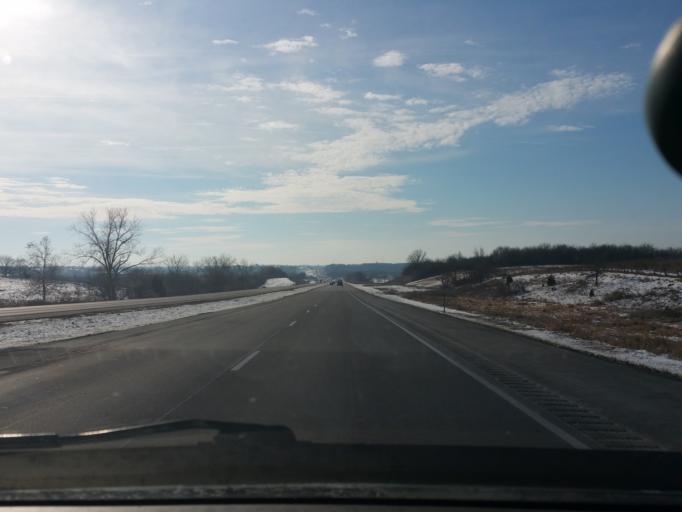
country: US
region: Iowa
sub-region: Warren County
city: Norwalk
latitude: 41.3851
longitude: -93.7809
